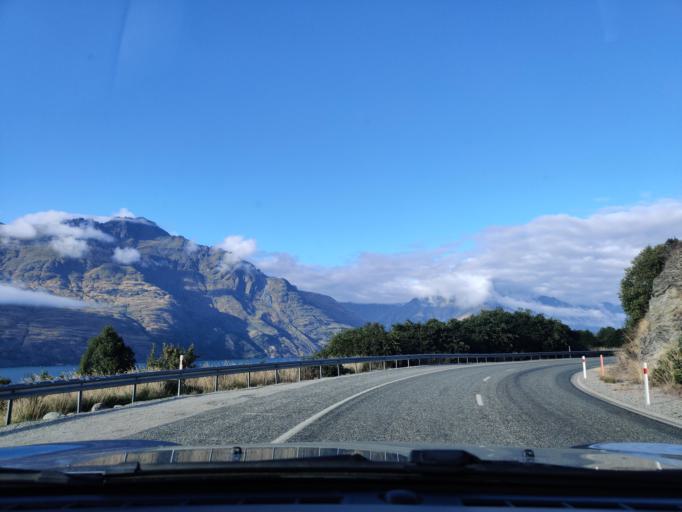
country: NZ
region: Otago
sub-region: Queenstown-Lakes District
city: Queenstown
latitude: -45.0527
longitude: 168.6190
